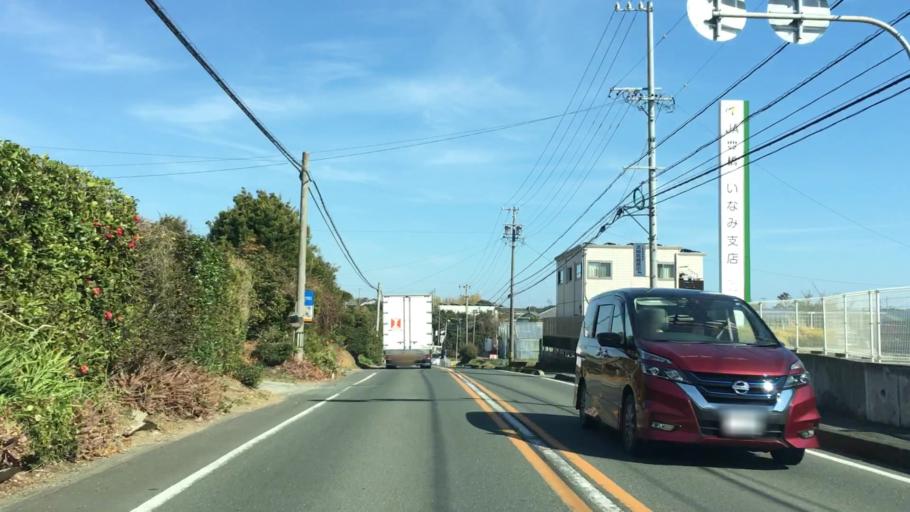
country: JP
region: Shizuoka
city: Kosai-shi
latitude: 34.6845
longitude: 137.4559
